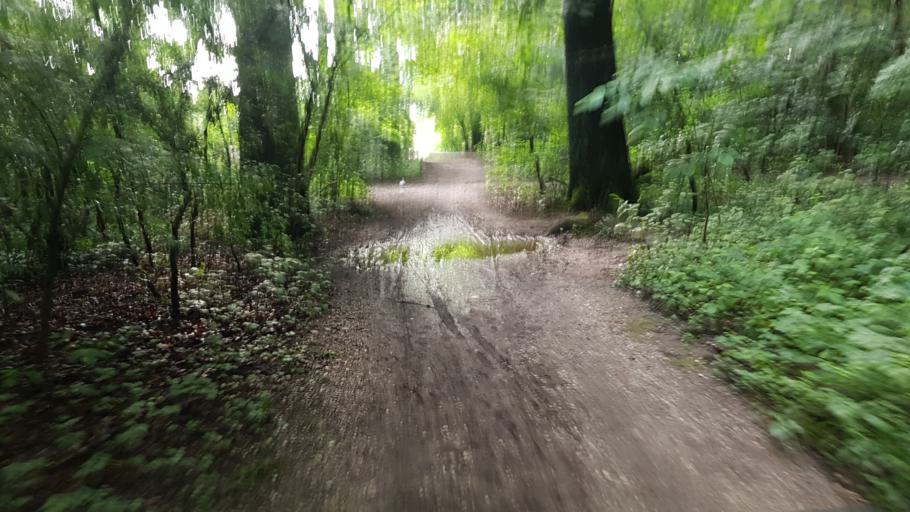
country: DE
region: Bavaria
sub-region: Upper Bavaria
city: Pasing
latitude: 48.1680
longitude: 11.4971
